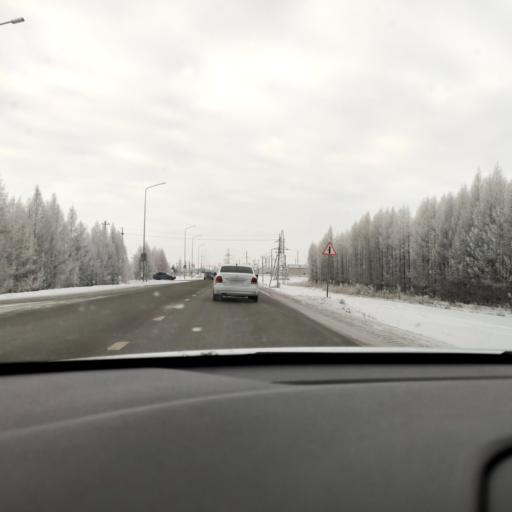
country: RU
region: Tatarstan
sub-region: Arskiy Rayon
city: Arsk
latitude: 56.1054
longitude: 49.8813
